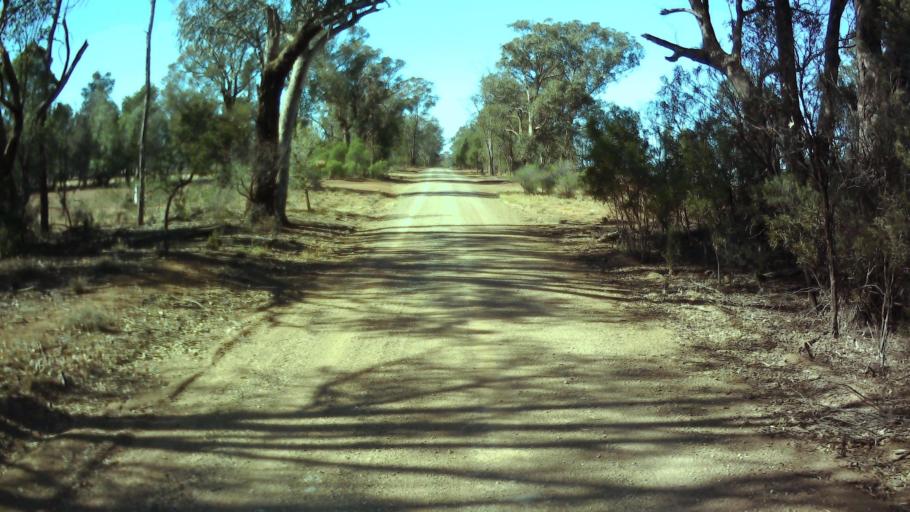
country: AU
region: New South Wales
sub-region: Weddin
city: Grenfell
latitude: -33.9251
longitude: 147.8740
